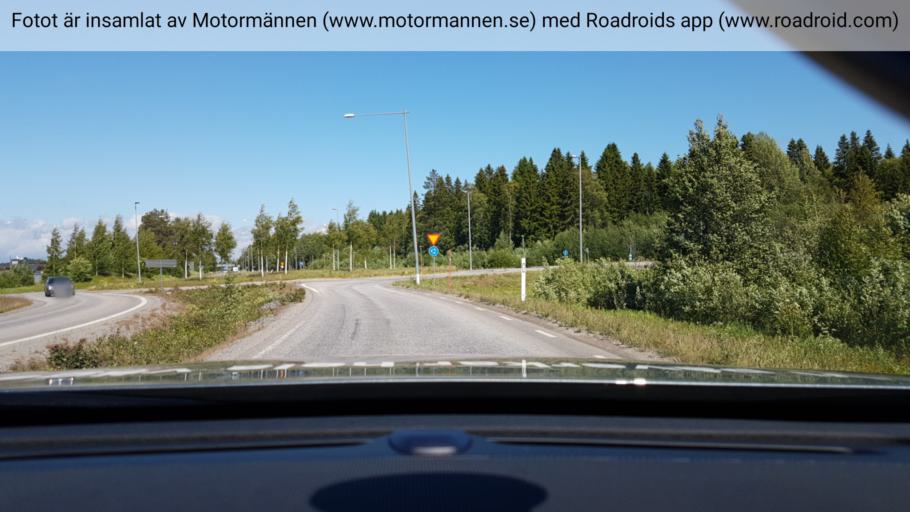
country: SE
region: Vaesterbotten
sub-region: Umea Kommun
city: Umea
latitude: 63.7922
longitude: 20.3121
